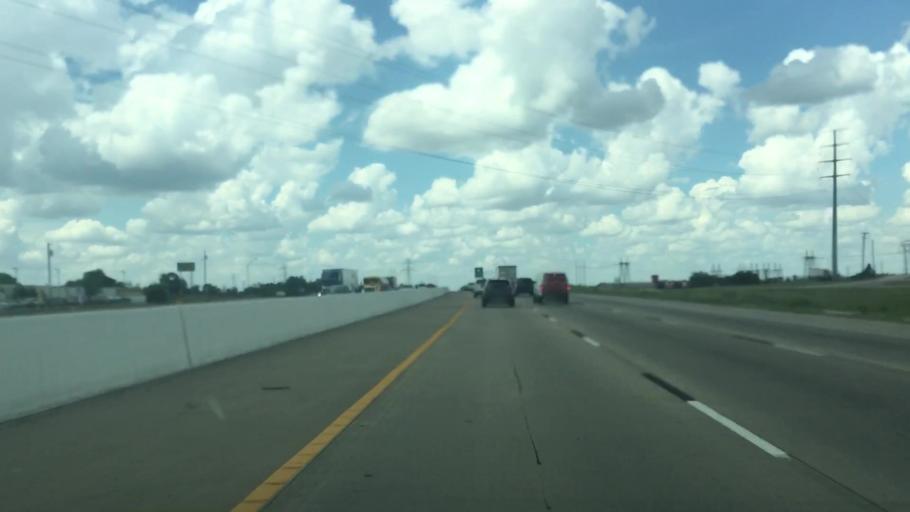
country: US
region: Texas
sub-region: McLennan County
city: Northcrest
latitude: 31.6935
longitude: -97.1006
